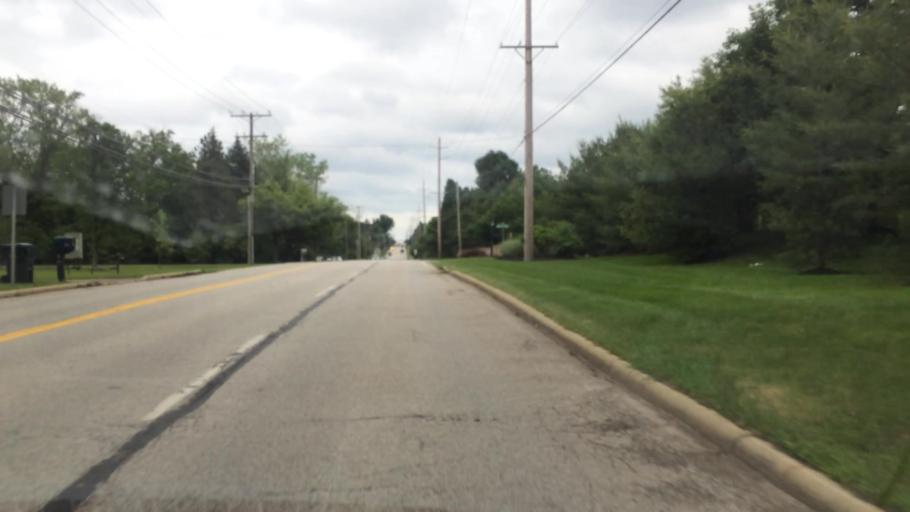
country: US
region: Ohio
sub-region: Summit County
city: Cuyahoga Falls
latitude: 41.1809
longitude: -81.5226
